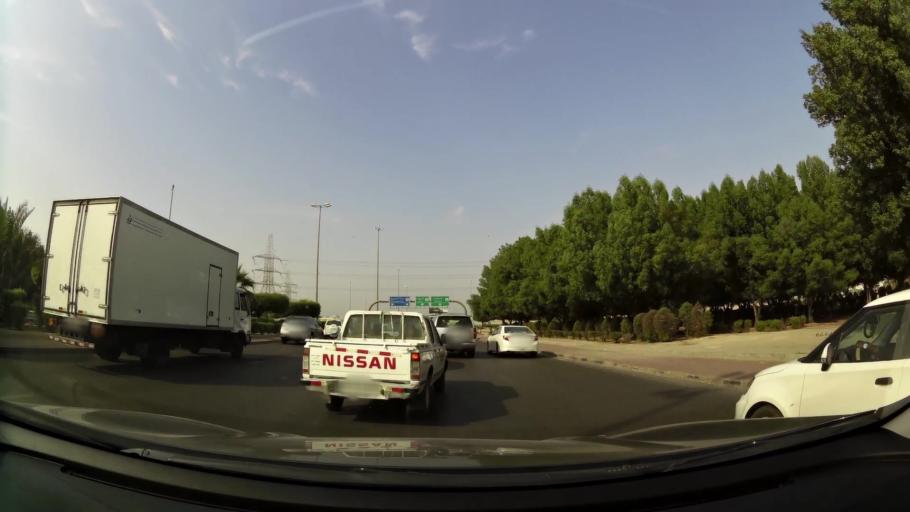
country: KW
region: Al Farwaniyah
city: Al Farwaniyah
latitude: 29.2995
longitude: 47.9644
